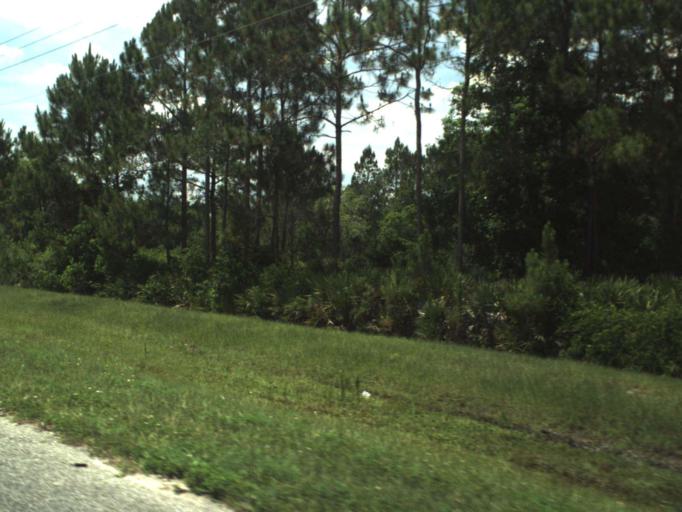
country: US
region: Florida
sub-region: Volusia County
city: Samsula-Spruce Creek
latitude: 29.0137
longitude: -81.0890
